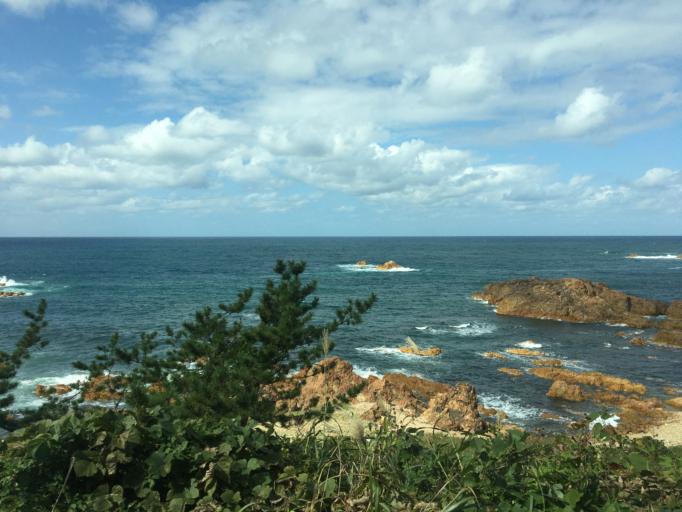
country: JP
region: Aomori
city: Shimokizukuri
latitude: 40.6648
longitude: 139.9396
